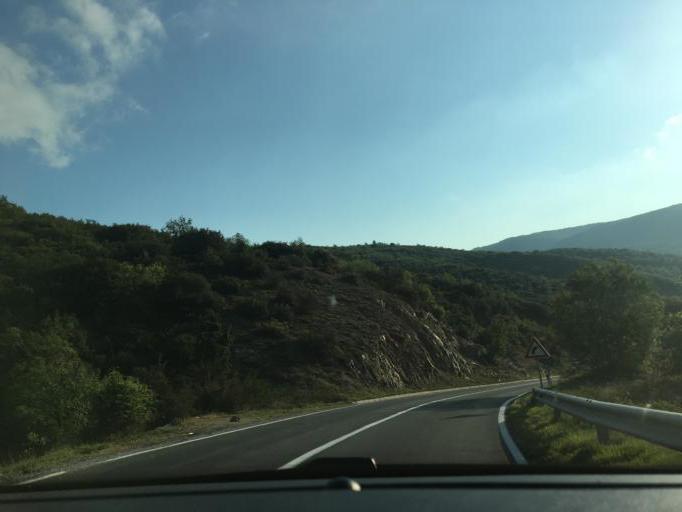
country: MK
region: Valandovo
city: Valandovo
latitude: 41.3218
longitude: 22.5975
